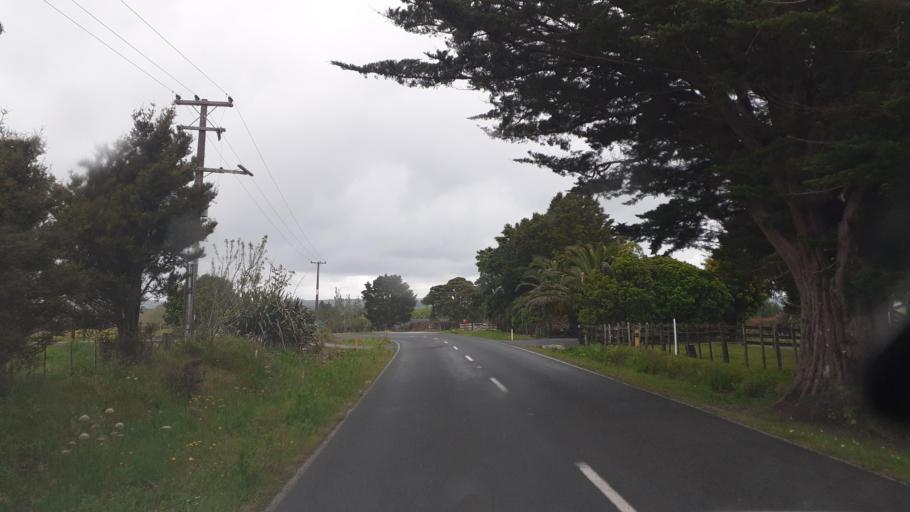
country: NZ
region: Northland
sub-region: Far North District
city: Waimate North
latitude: -35.2768
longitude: 173.8305
